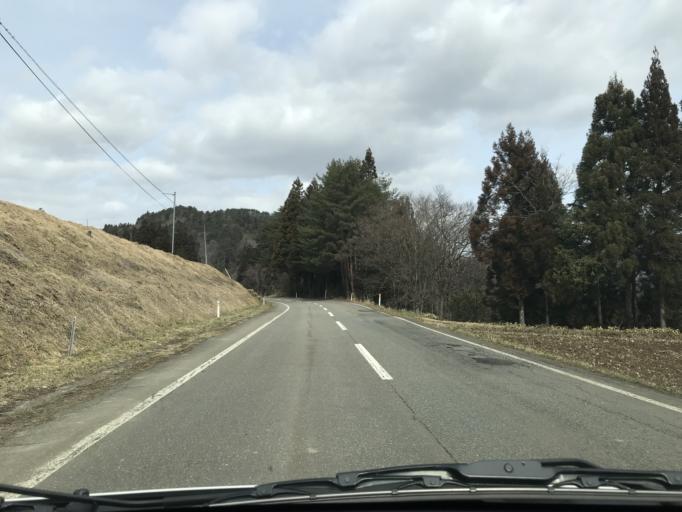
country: JP
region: Iwate
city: Kitakami
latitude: 39.2785
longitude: 141.3202
